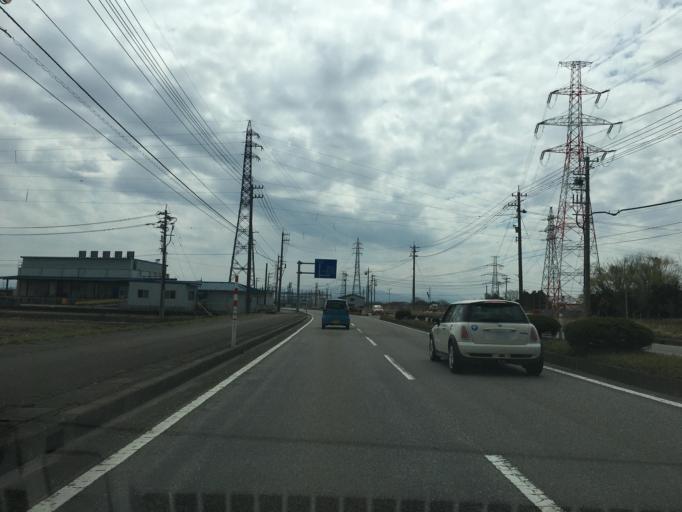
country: JP
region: Toyama
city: Kuragaki-kosugi
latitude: 36.7491
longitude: 137.1300
